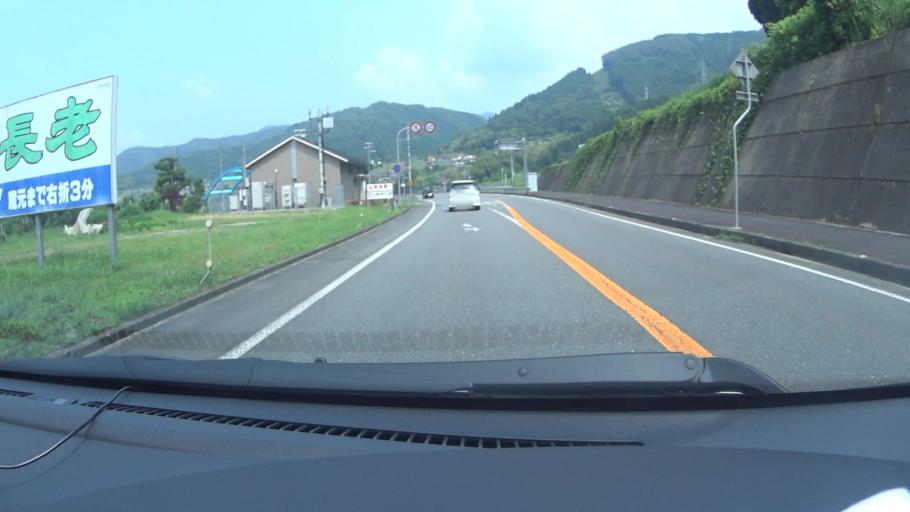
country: JP
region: Kyoto
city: Ayabe
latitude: 35.2674
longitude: 135.4016
